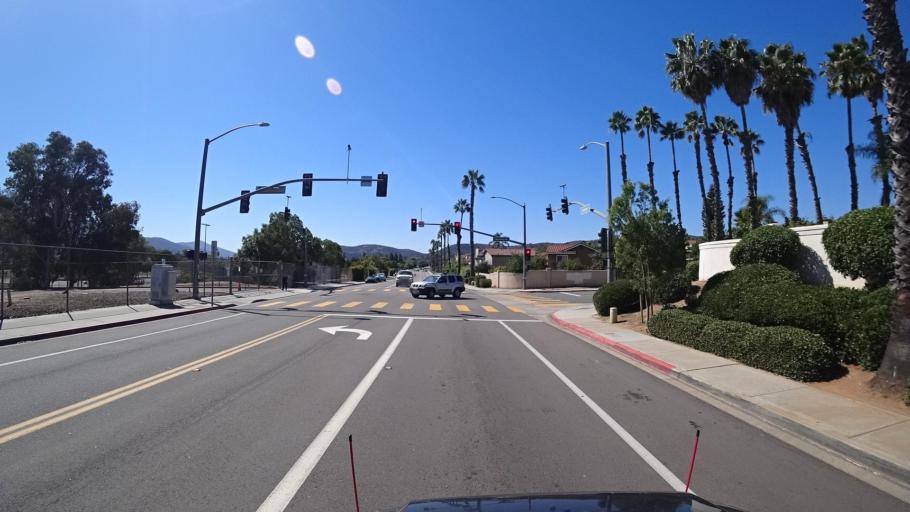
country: US
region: California
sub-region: San Diego County
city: Rancho San Diego
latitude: 32.7491
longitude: -116.9340
